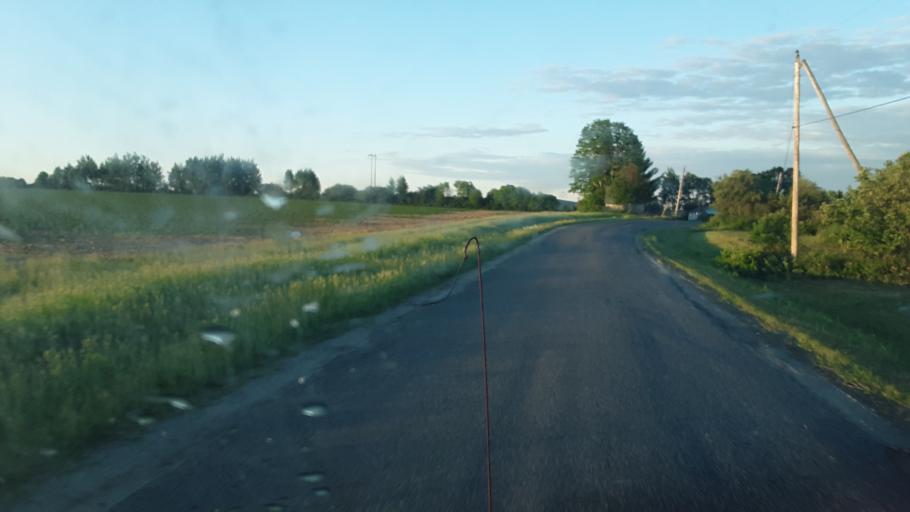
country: US
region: Maine
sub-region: Aroostook County
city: Caribou
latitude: 46.7811
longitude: -68.0989
